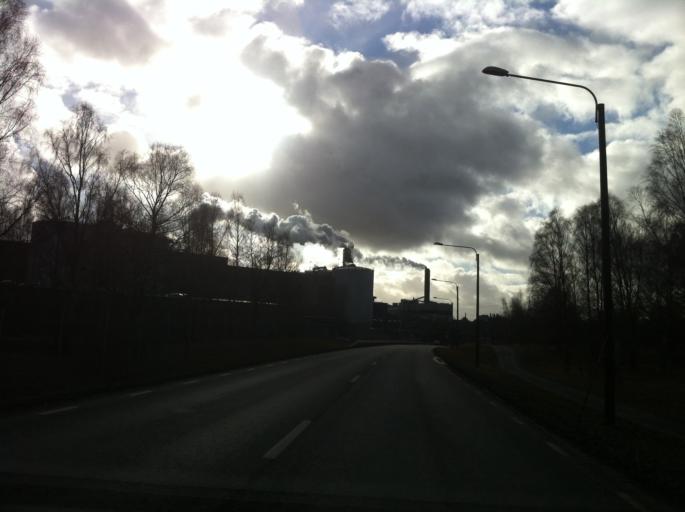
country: SE
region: Blekinge
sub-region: Solvesborgs Kommun
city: Soelvesborg
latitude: 56.0633
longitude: 14.5406
